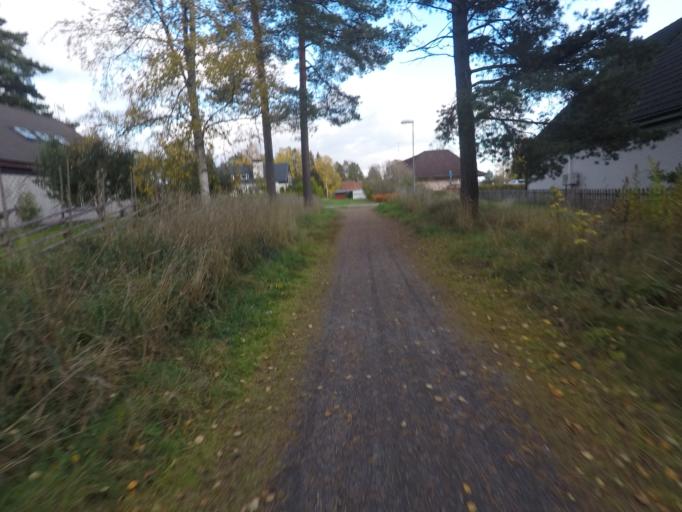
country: SE
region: OErebro
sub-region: Karlskoga Kommun
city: Karlskoga
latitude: 59.3063
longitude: 14.4918
